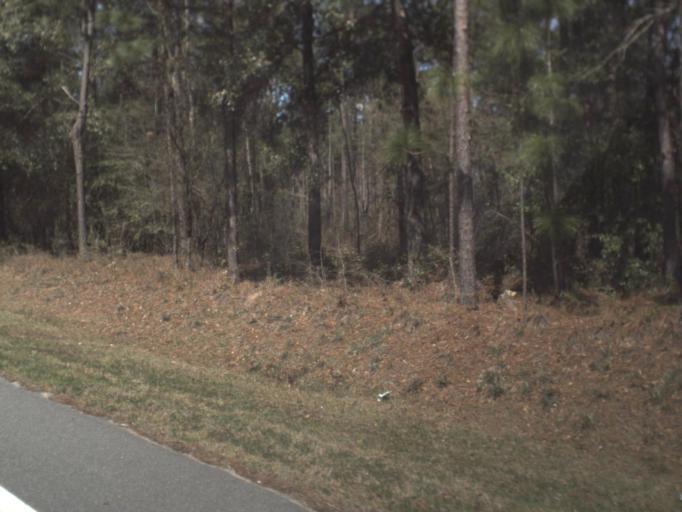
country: US
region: Florida
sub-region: Gadsden County
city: Gretna
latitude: 30.6716
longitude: -84.7018
